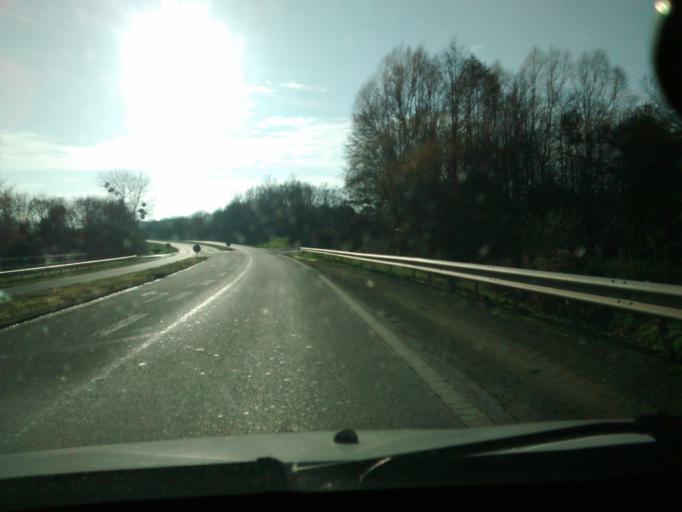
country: FR
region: Brittany
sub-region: Departement d'Ille-et-Vilaine
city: Sens-de-Bretagne
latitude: 48.3525
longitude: -1.5166
